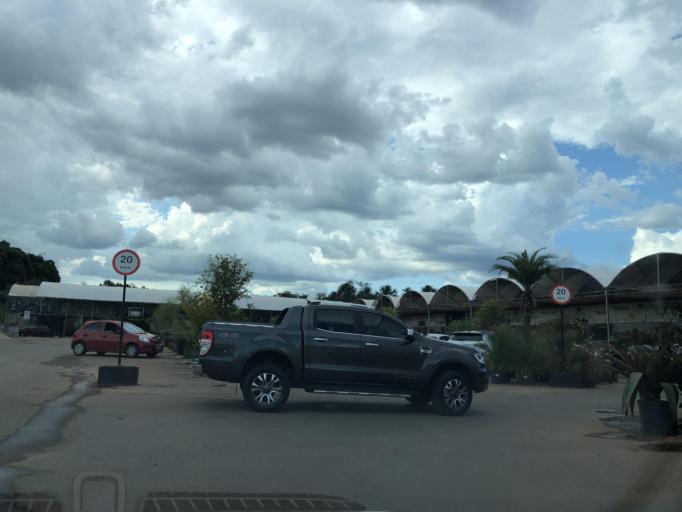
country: BR
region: Federal District
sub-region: Brasilia
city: Brasilia
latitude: -15.8142
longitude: -48.0091
